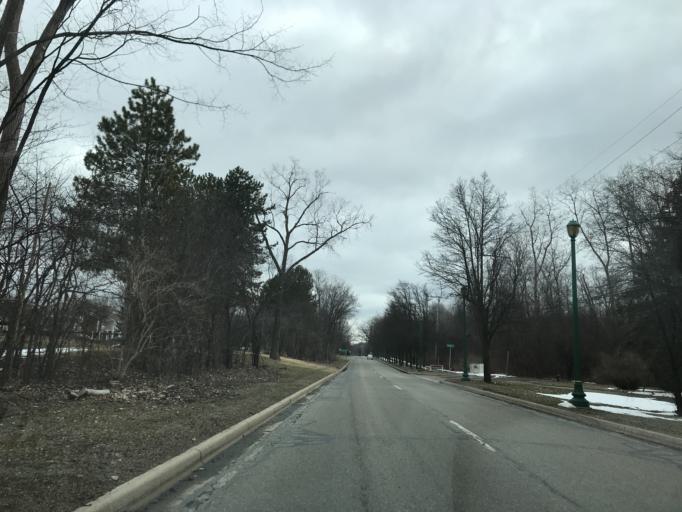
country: US
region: Michigan
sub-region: Oakland County
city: Bingham Farms
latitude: 42.4791
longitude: -83.2734
